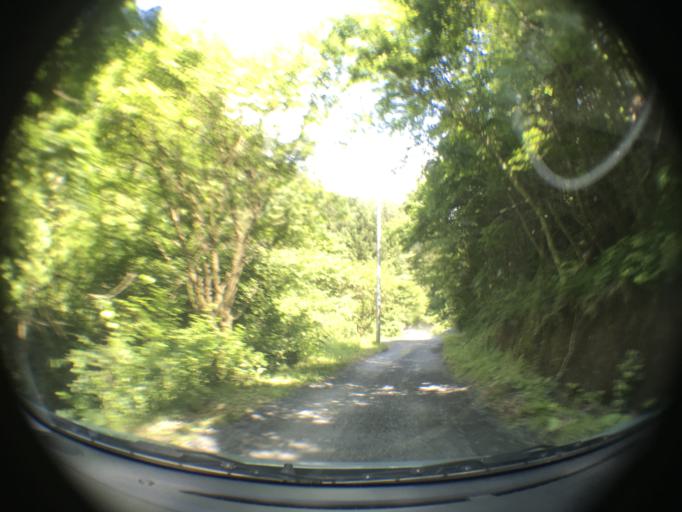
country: JP
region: Iwate
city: Ichinoseki
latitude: 38.7791
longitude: 141.4193
